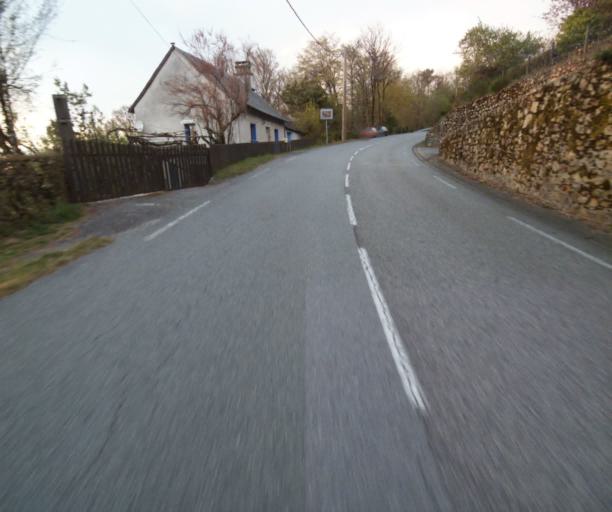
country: FR
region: Limousin
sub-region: Departement de la Correze
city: Laguenne
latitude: 45.2851
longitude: 1.8458
